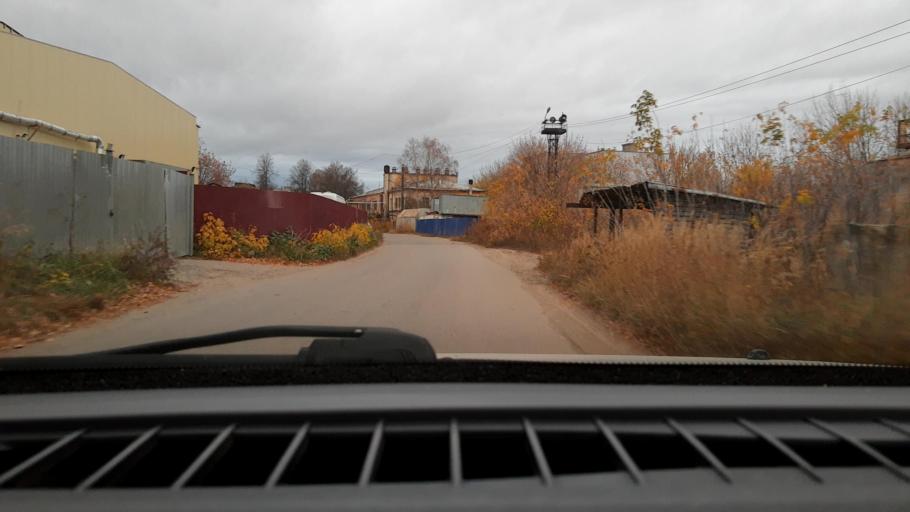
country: RU
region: Nizjnij Novgorod
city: Nizhniy Novgorod
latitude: 56.3357
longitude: 43.8920
